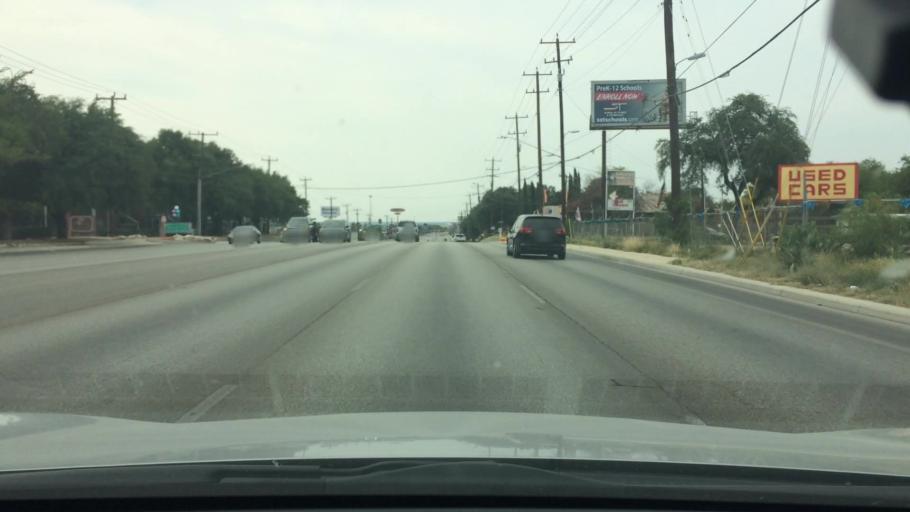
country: US
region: Texas
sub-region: Bexar County
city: Leon Valley
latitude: 29.4610
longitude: -98.6405
